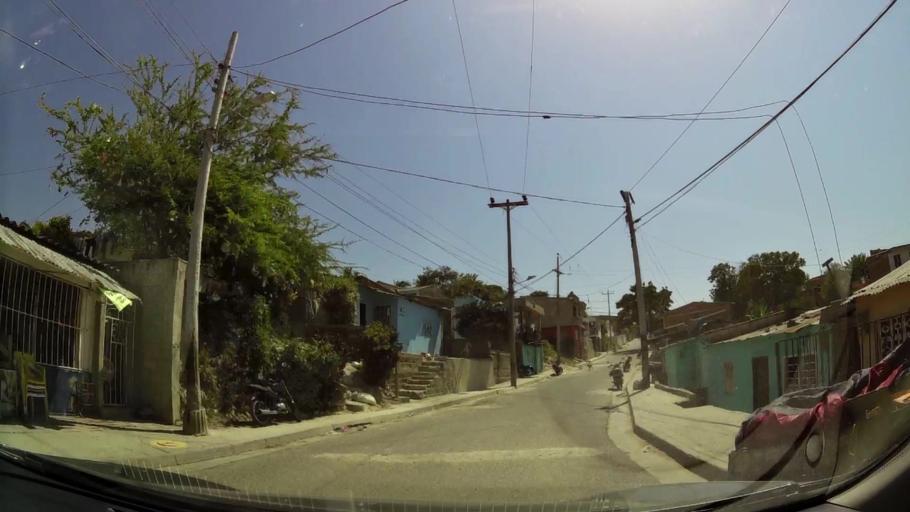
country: CO
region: Bolivar
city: Cartagena
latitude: 10.4303
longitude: -75.5257
